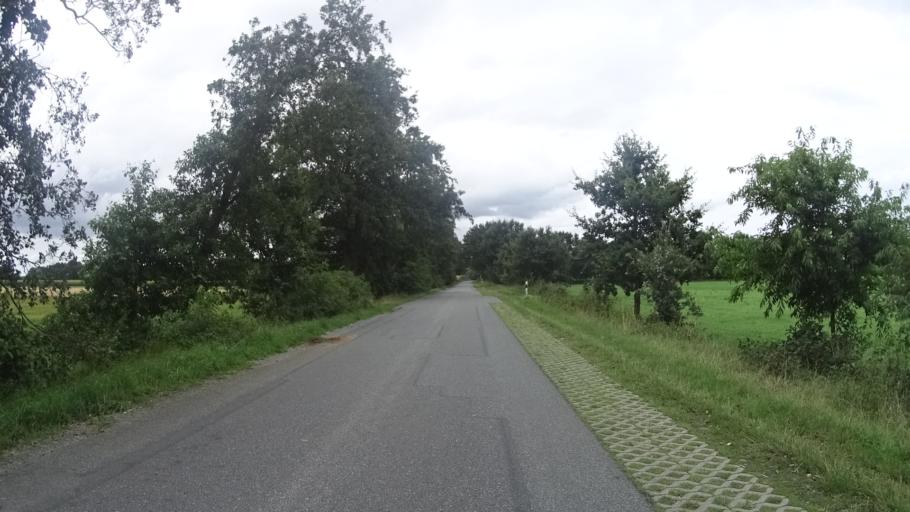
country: DE
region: Lower Saxony
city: Stinstedt
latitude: 53.6501
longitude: 8.9619
